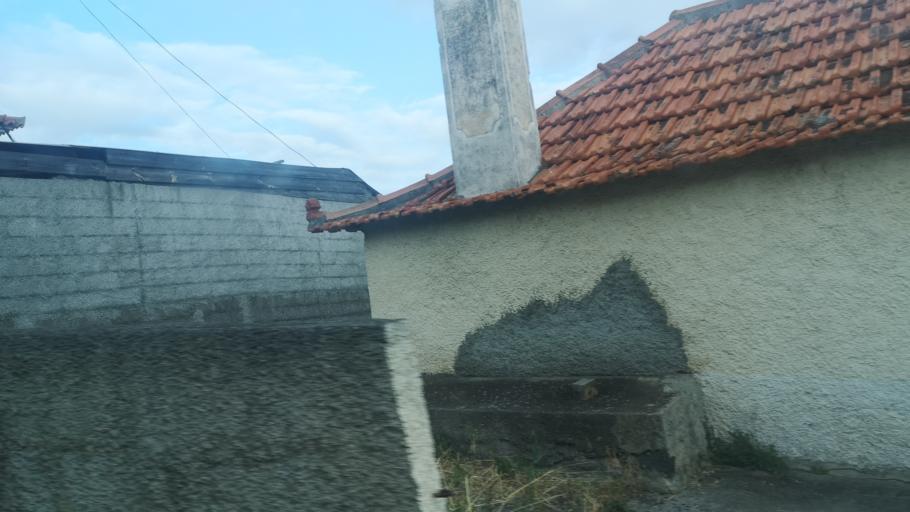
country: PT
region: Madeira
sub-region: Santa Cruz
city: Santa Cruz
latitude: 32.6574
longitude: -16.8149
